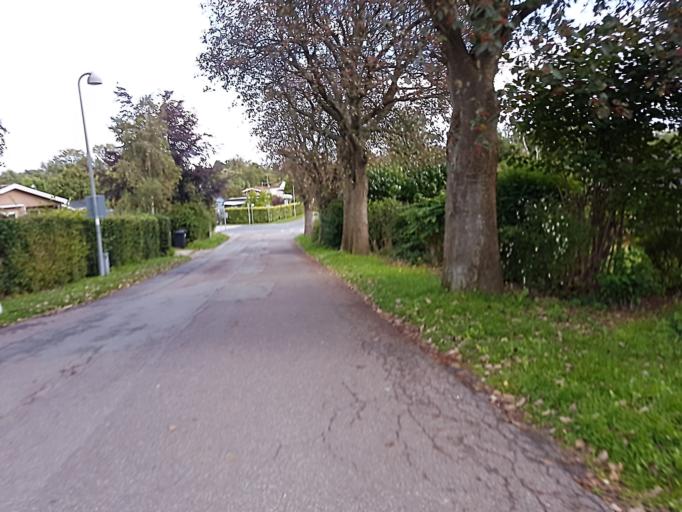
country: DK
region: Zealand
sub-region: Roskilde Kommune
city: Jyllinge
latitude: 55.7646
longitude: 12.0958
